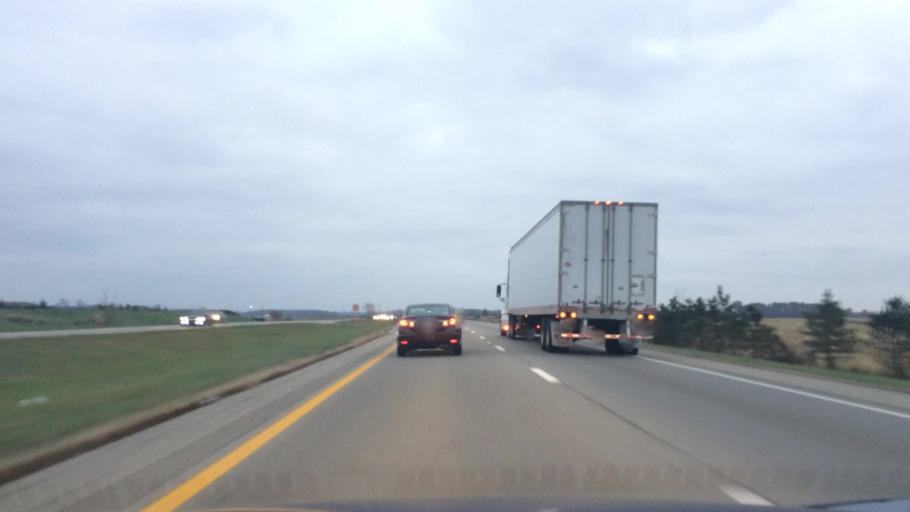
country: US
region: Ohio
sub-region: Union County
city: New California
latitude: 40.1952
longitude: -83.2737
